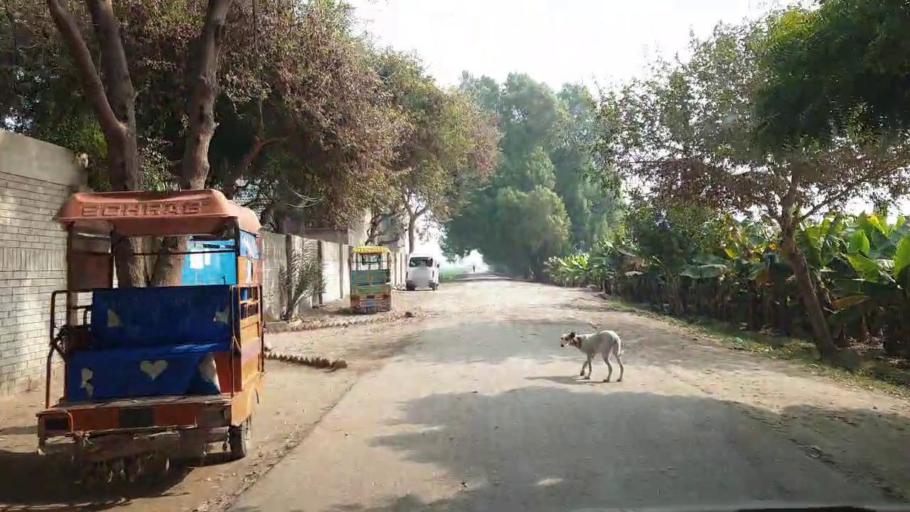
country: PK
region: Sindh
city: Hala
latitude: 25.8253
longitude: 68.4320
